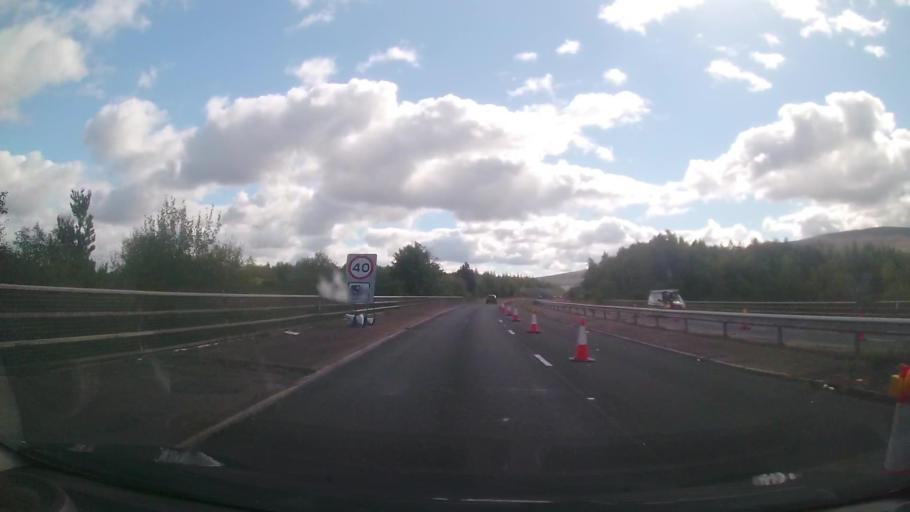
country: GB
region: Wales
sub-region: Rhondda Cynon Taf
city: Hirwaun
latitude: 51.7444
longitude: -3.5309
